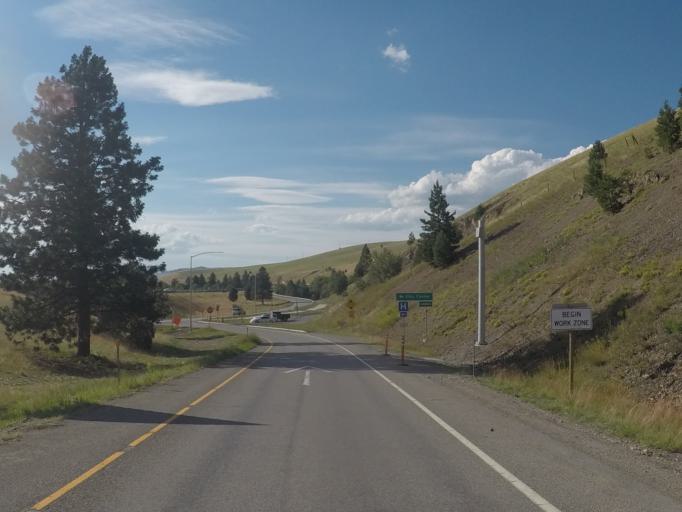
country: US
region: Montana
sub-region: Missoula County
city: Missoula
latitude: 46.8798
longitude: -113.9915
